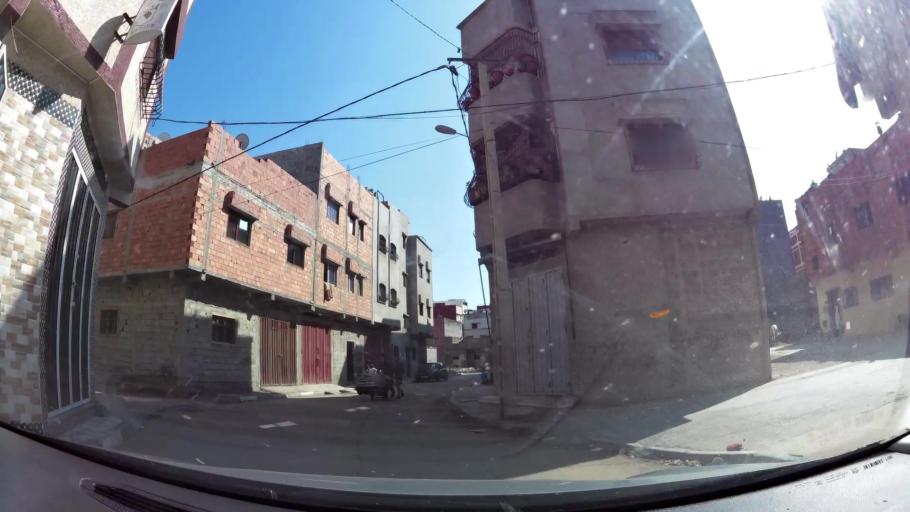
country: MA
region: Rabat-Sale-Zemmour-Zaer
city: Sale
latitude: 34.0596
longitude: -6.7713
